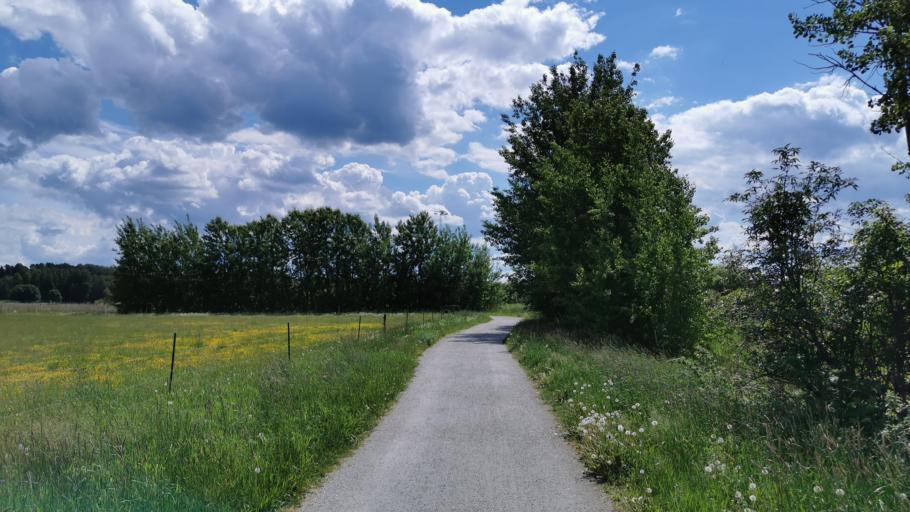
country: SE
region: OErebro
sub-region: Orebro Kommun
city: Orebro
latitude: 59.3005
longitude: 15.2092
